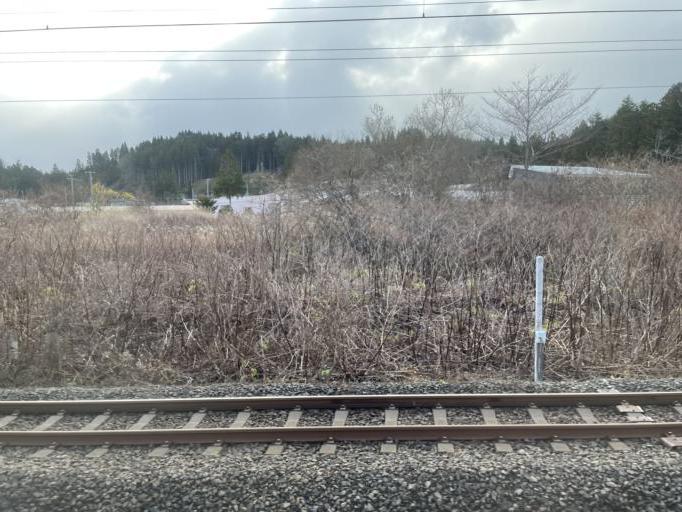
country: JP
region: Aomori
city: Aomori Shi
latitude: 41.0404
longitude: 140.6400
